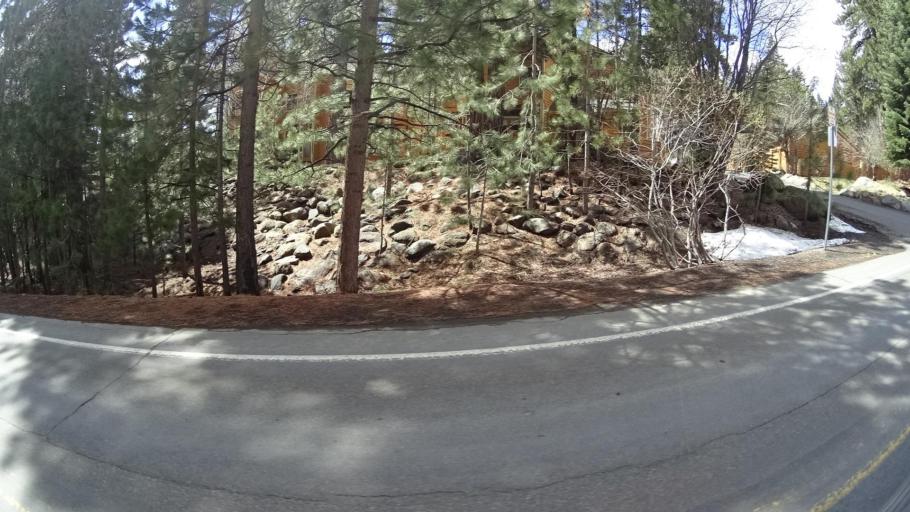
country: US
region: Nevada
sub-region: Washoe County
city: Incline Village
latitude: 39.2444
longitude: -119.9459
